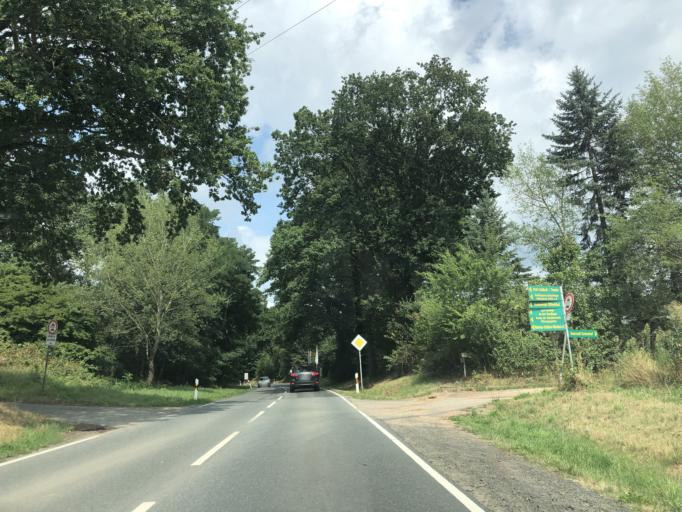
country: DE
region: Hesse
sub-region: Regierungsbezirk Darmstadt
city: Dietzenbach
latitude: 49.9852
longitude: 8.7565
